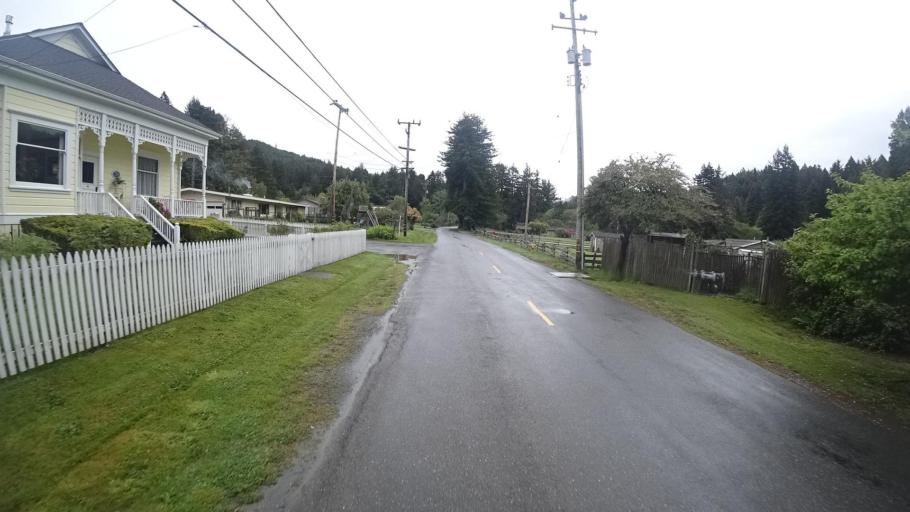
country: US
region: California
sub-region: Humboldt County
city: Bayside
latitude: 40.8315
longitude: -124.0415
